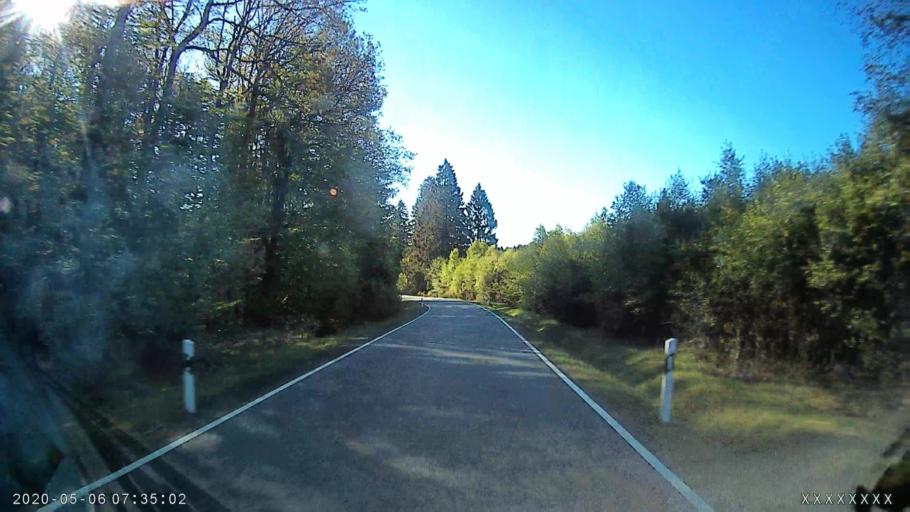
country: DE
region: Hesse
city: Dillenburg
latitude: 50.8207
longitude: 8.2519
